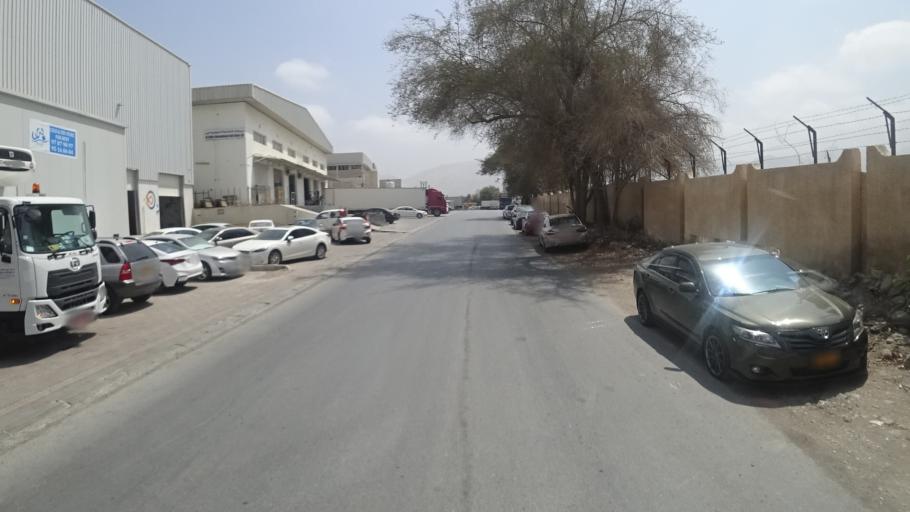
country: OM
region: Muhafazat Masqat
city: Bawshar
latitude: 23.5777
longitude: 58.3699
